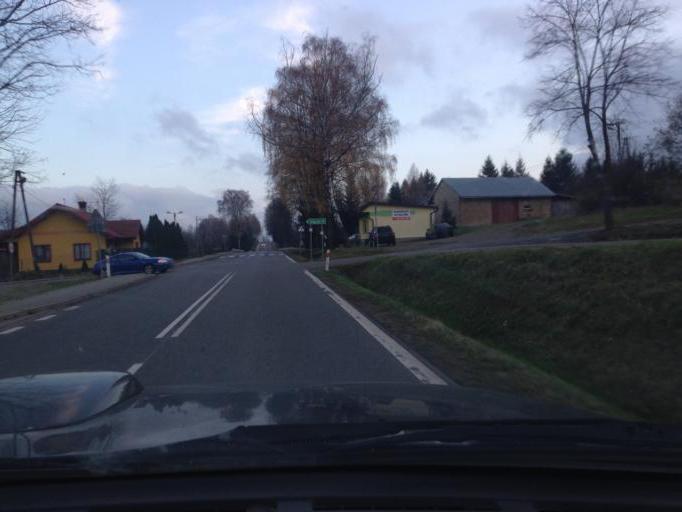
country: PL
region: Subcarpathian Voivodeship
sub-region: Powiat jasielski
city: Osiek Jasielski
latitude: 49.6425
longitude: 21.5175
